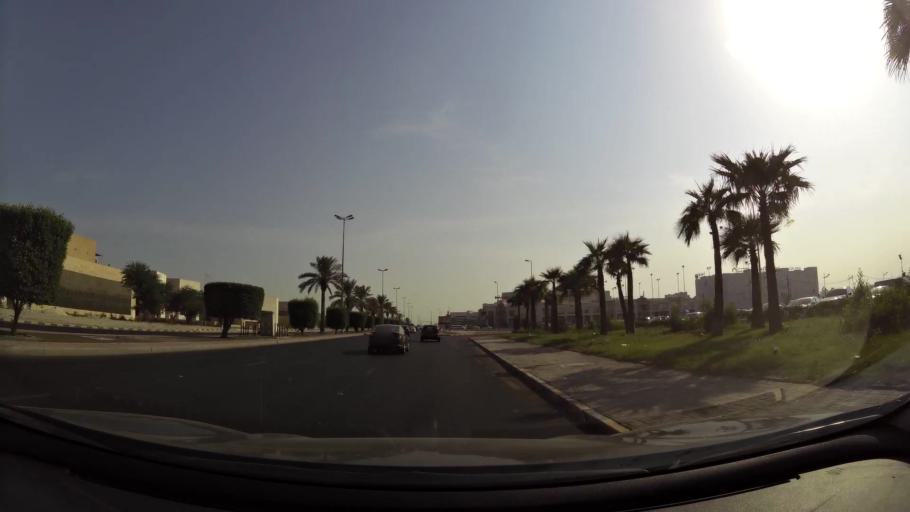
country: KW
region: Al Ahmadi
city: Al Fintas
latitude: 29.1727
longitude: 48.0999
